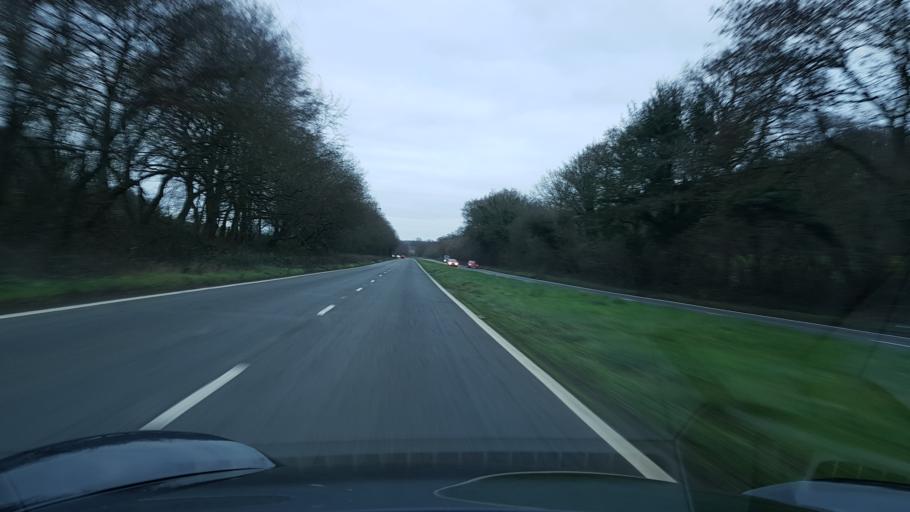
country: GB
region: England
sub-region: Hampshire
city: Alton
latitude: 51.1275
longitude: -1.0096
